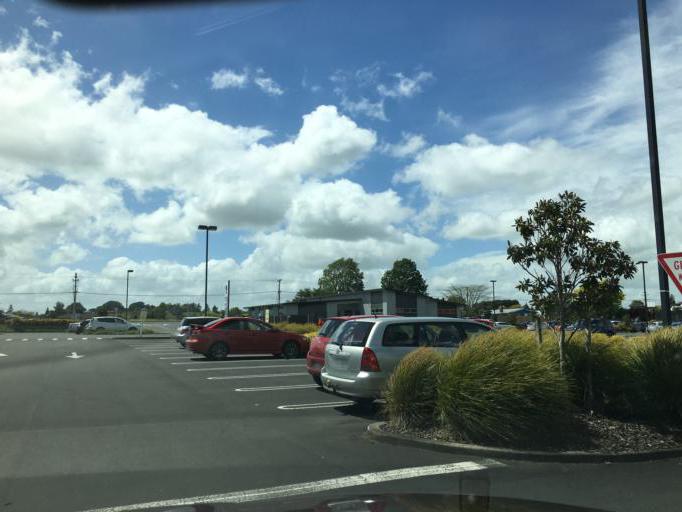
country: NZ
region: Waikato
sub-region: Waipa District
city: Cambridge
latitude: -38.0075
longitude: 175.3399
